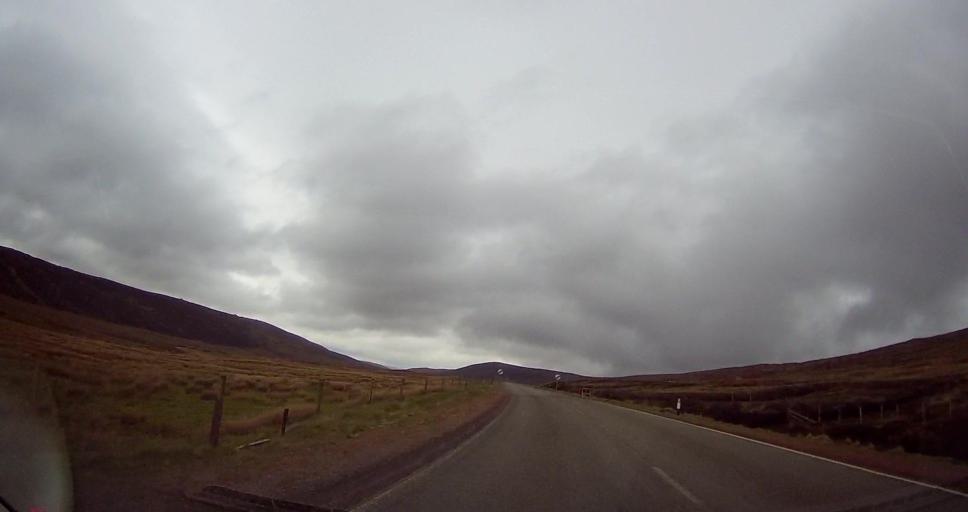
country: GB
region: Scotland
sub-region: Shetland Islands
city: Lerwick
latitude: 60.2804
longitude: -1.2445
